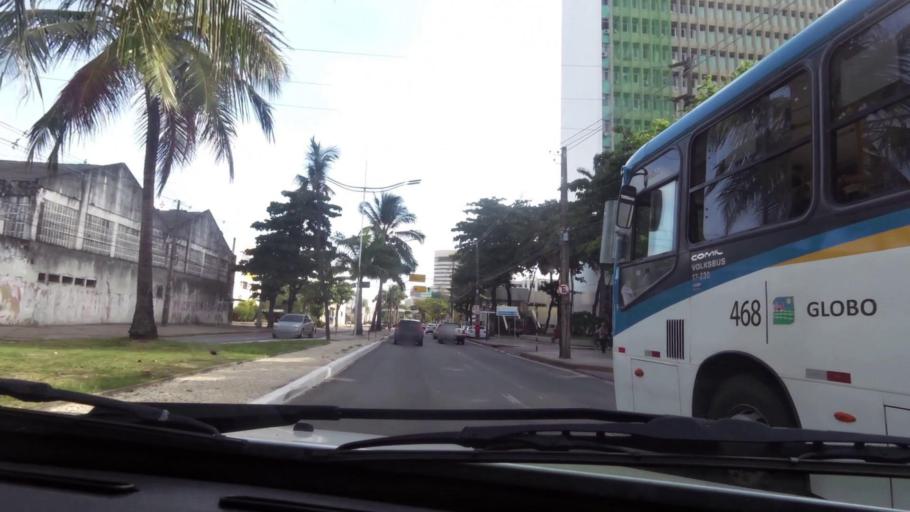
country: BR
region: Pernambuco
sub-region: Recife
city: Recife
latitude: -8.0550
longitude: -34.8721
